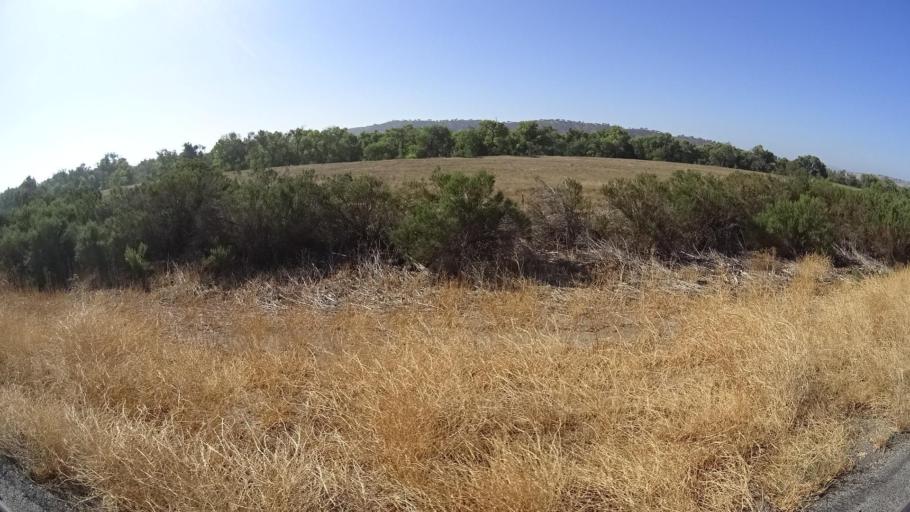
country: US
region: California
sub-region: San Luis Obispo County
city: San Miguel
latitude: 35.8623
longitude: -120.7751
